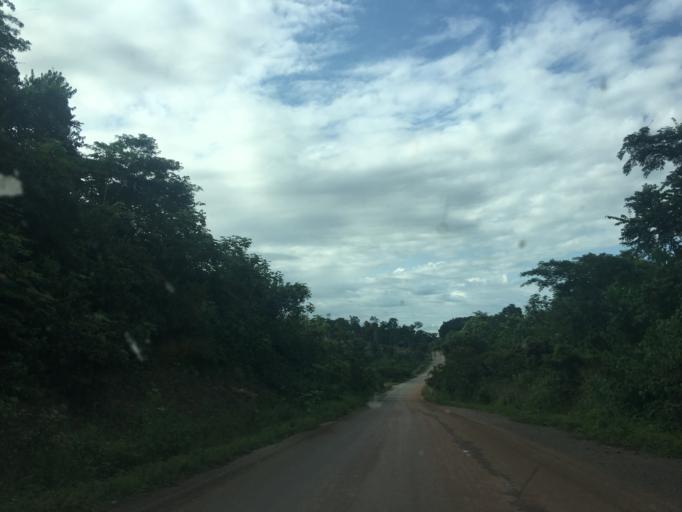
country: GH
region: Western
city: Wassa-Akropong
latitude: 5.9854
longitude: -2.4132
